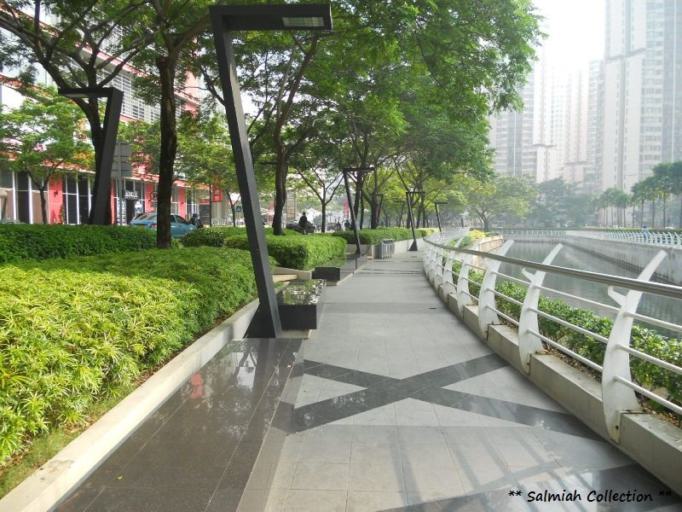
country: ID
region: Jakarta Raya
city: Jakarta
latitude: -6.2186
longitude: 106.8354
